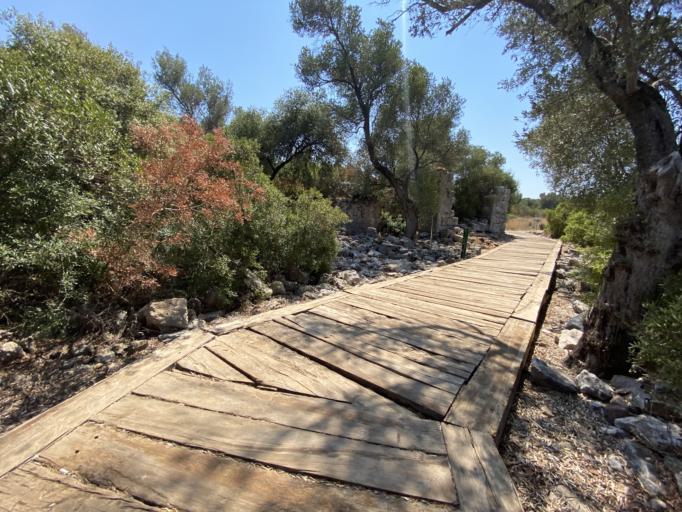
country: TR
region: Mugla
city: Yerkesik
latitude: 36.9918
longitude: 28.2055
